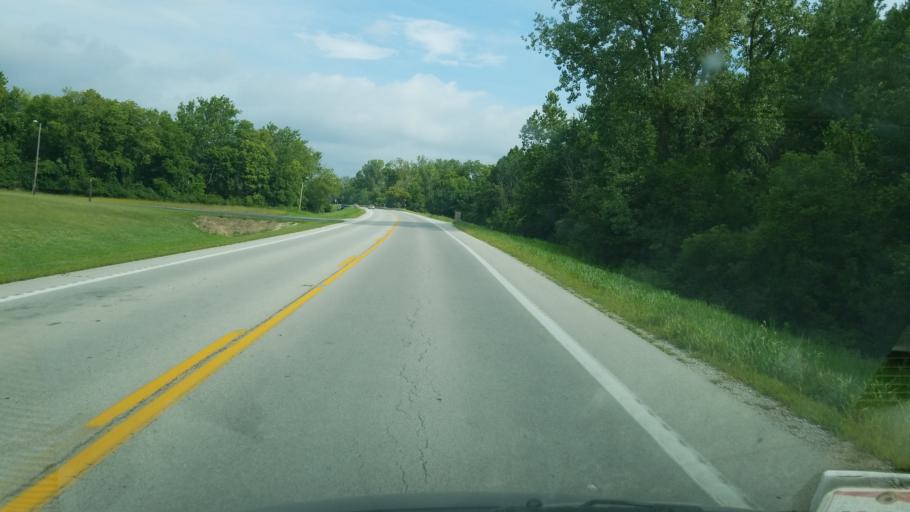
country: US
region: Ohio
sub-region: Sandusky County
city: Ballville
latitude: 41.2778
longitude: -83.1685
